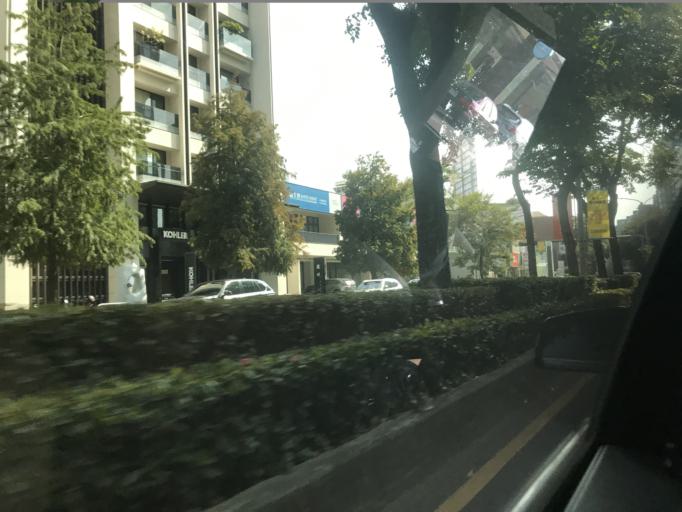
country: TW
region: Taiwan
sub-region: Taichung City
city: Taichung
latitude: 24.1497
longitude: 120.6377
